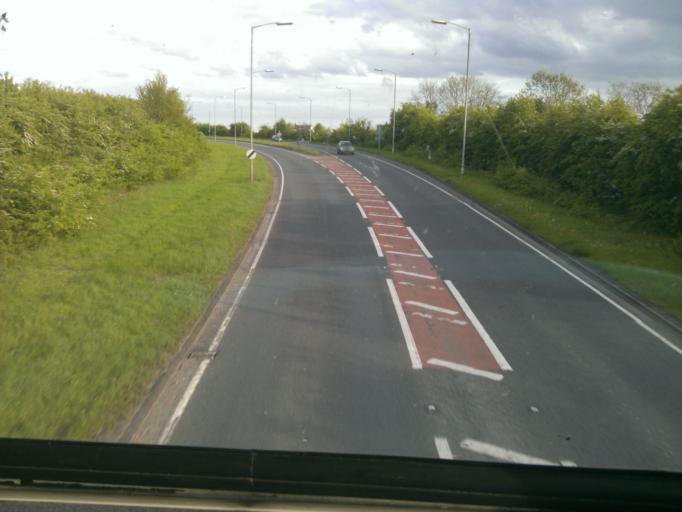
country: GB
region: England
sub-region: Essex
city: Coggeshall
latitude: 51.8753
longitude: 0.7004
